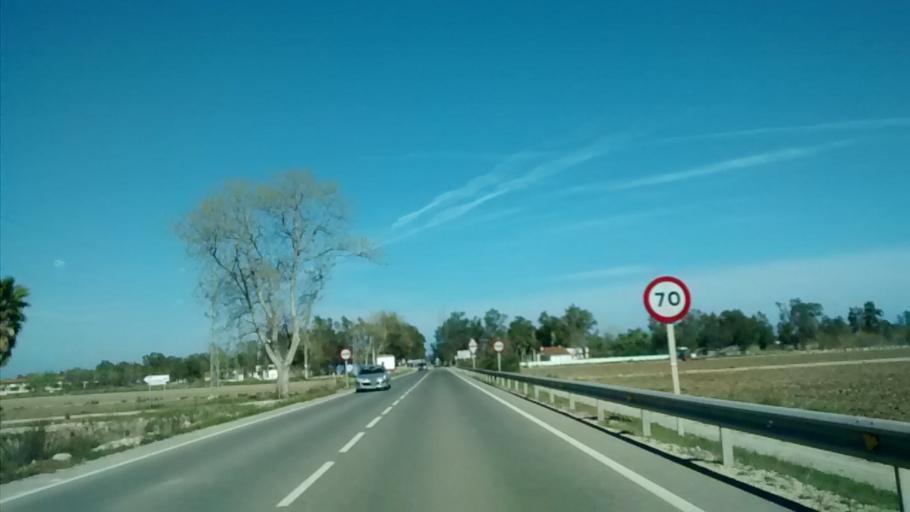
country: ES
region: Catalonia
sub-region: Provincia de Tarragona
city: Deltebre
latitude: 40.7134
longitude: 0.8248
